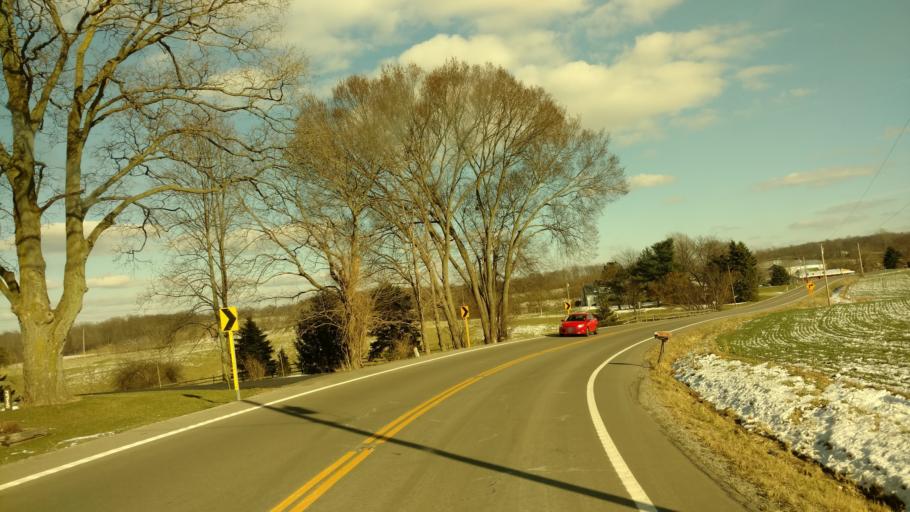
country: US
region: Ohio
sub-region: Ashland County
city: Loudonville
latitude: 40.7405
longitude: -82.2439
